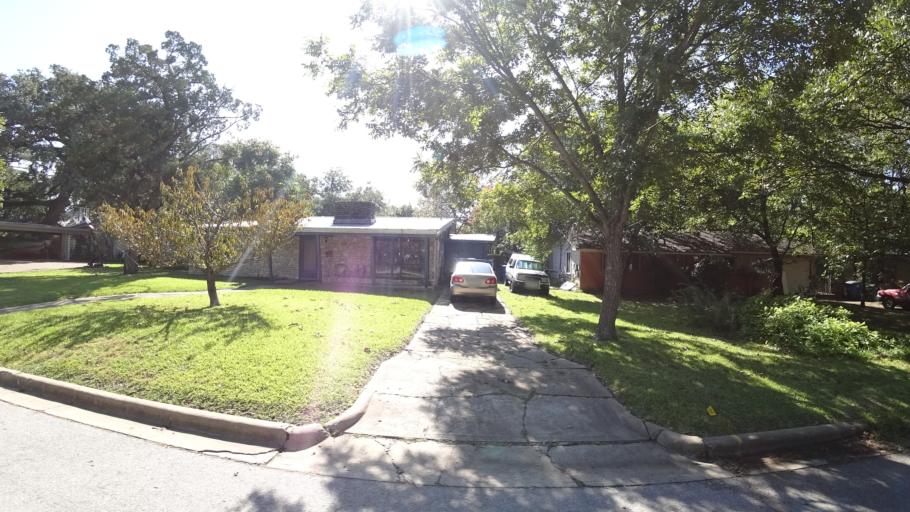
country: US
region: Texas
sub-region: Travis County
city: Austin
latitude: 30.2591
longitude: -97.7673
